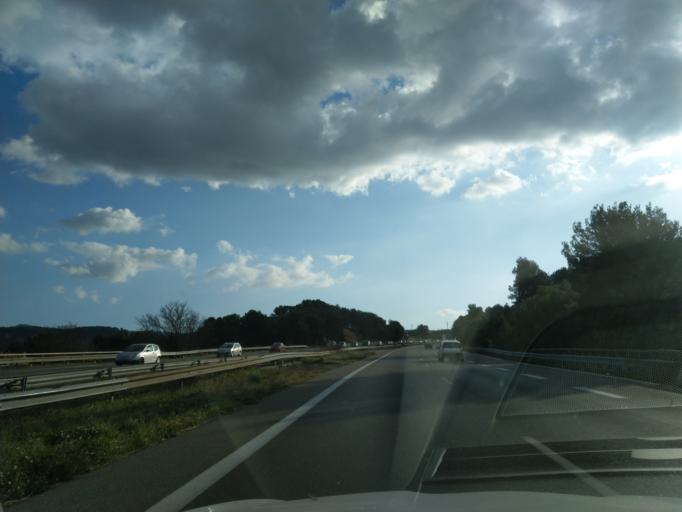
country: FR
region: Provence-Alpes-Cote d'Azur
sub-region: Departement des Bouches-du-Rhone
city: Cabries
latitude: 43.4385
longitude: 5.3962
